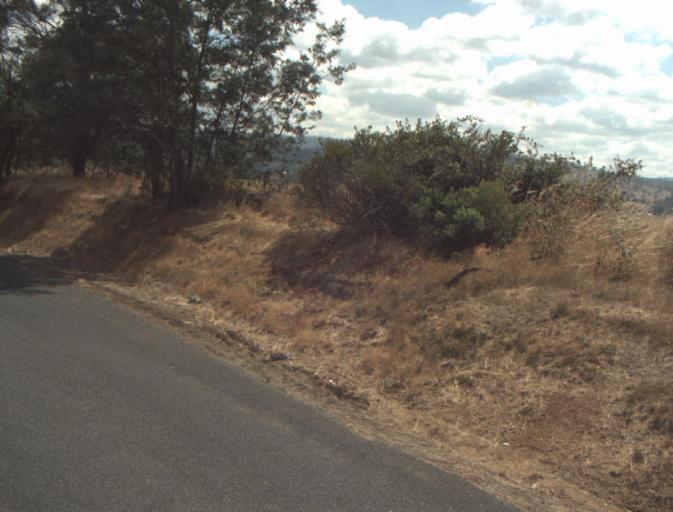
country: AU
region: Tasmania
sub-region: Launceston
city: Newstead
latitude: -41.4783
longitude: 147.1900
